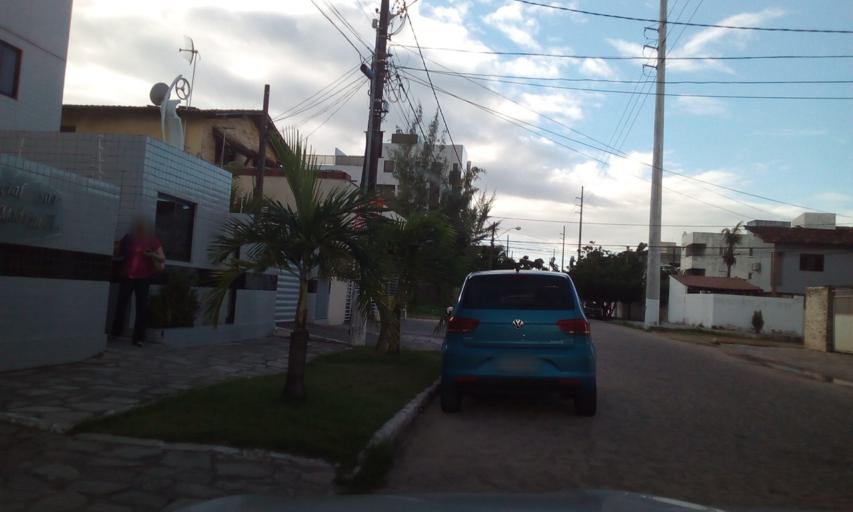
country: BR
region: Paraiba
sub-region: Joao Pessoa
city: Joao Pessoa
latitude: -7.0716
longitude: -34.8456
